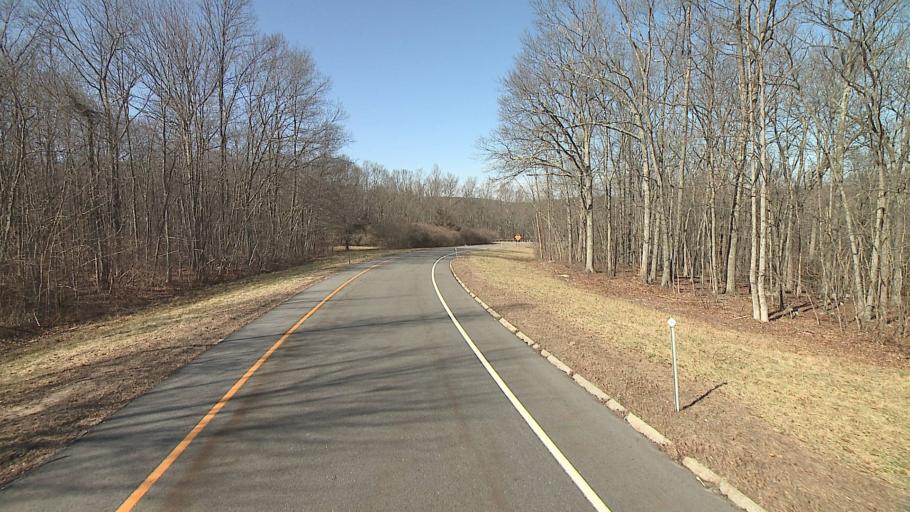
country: US
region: Connecticut
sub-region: New London County
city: Colchester
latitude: 41.5724
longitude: -72.2949
